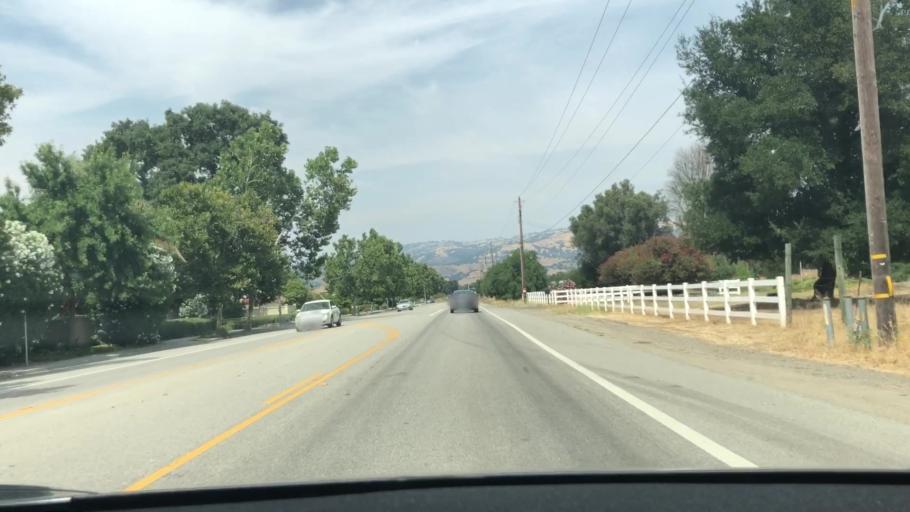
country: US
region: California
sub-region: Santa Clara County
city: Morgan Hill
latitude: 37.1030
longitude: -121.6395
